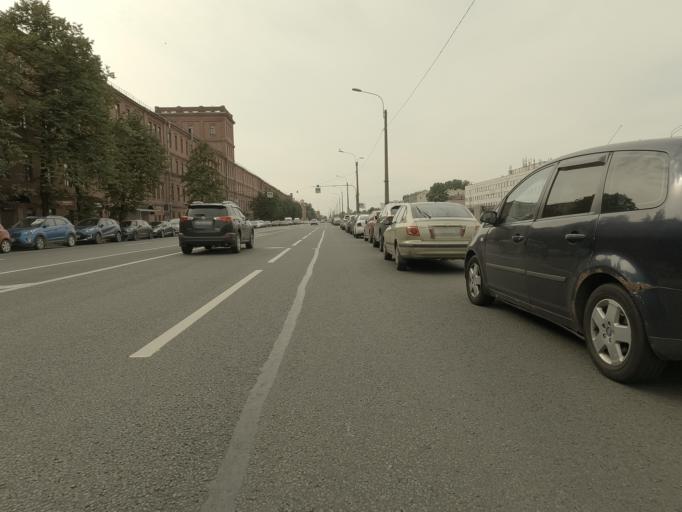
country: RU
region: St.-Petersburg
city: Admiralteisky
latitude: 59.9089
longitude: 30.2835
